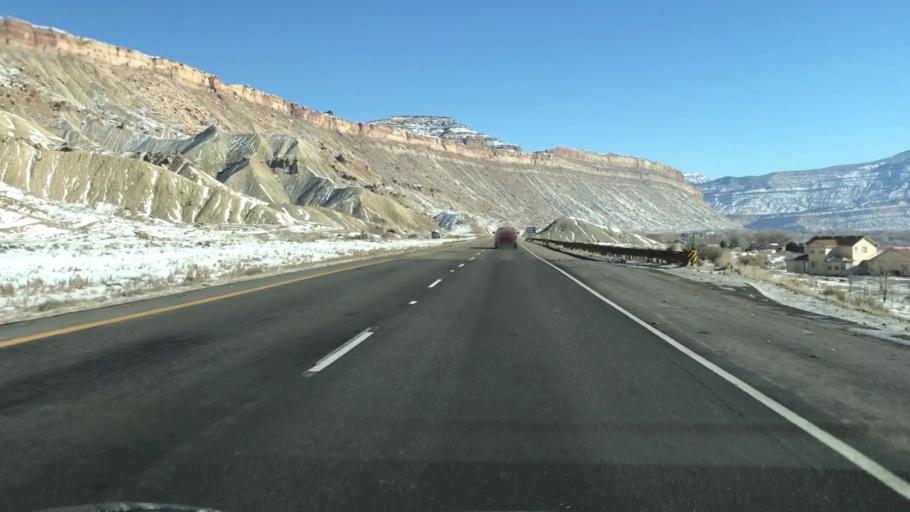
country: US
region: Colorado
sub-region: Mesa County
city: Palisade
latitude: 39.1153
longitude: -108.3983
